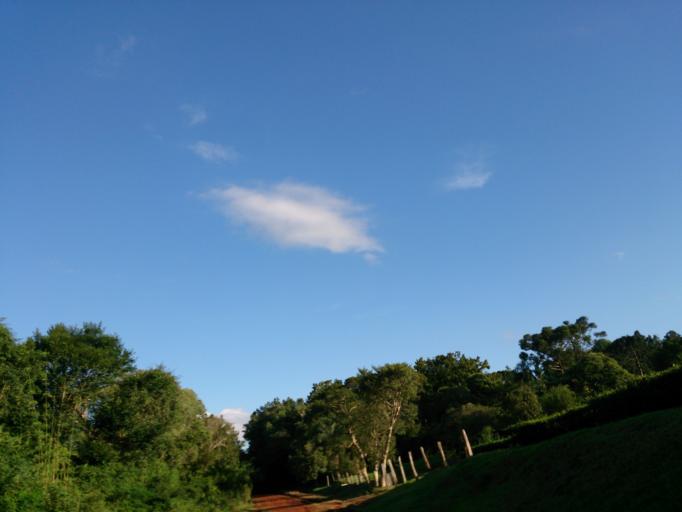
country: AR
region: Misiones
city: Guarani
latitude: -27.5558
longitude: -55.1812
